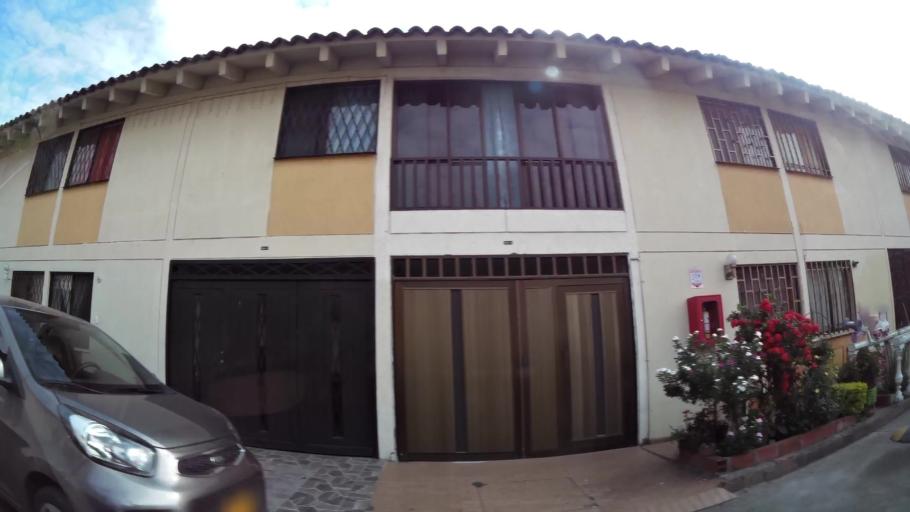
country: CO
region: Valle del Cauca
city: Cali
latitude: 3.4828
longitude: -76.4930
